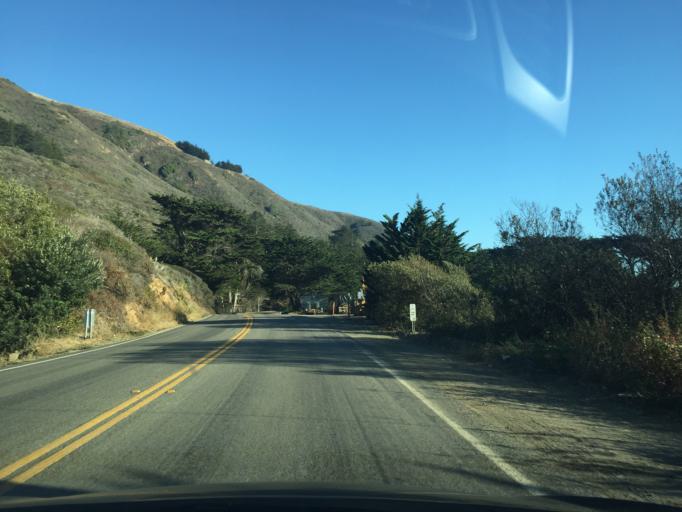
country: US
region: California
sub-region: San Luis Obispo County
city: Cambria
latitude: 35.7831
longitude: -121.3309
